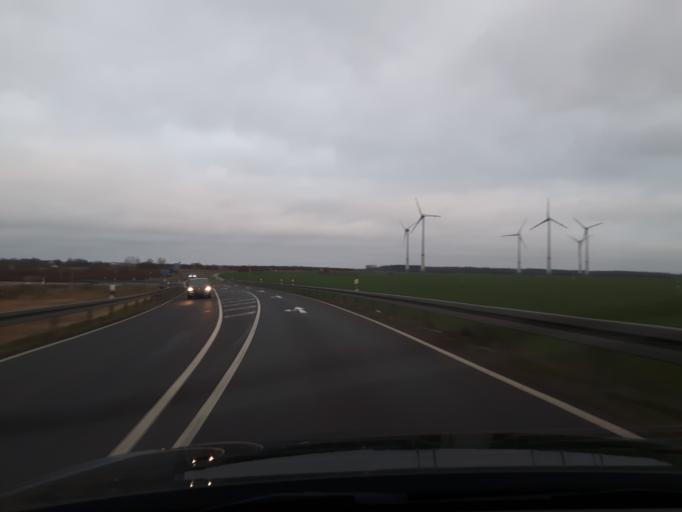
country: DE
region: Mecklenburg-Vorpommern
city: Tribsees
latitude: 54.0789
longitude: 12.7546
